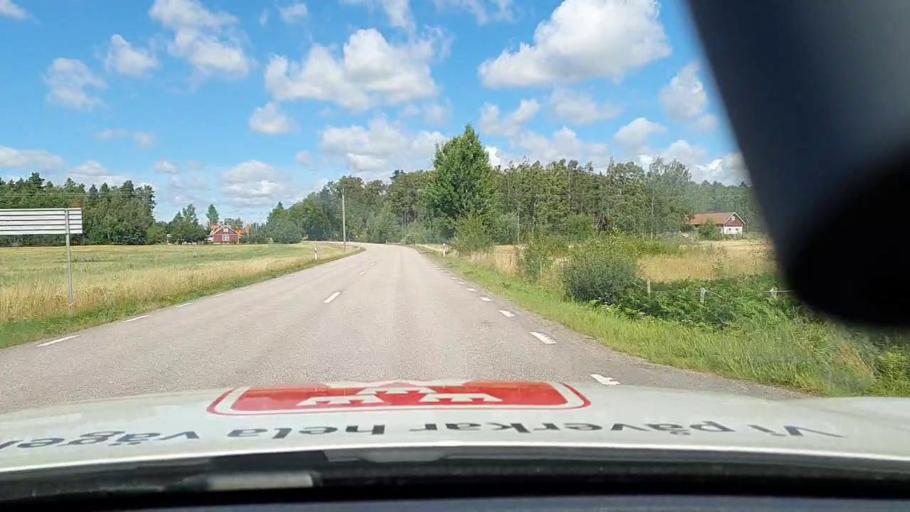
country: SE
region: Vaestra Goetaland
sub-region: Skovde Kommun
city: Stopen
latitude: 58.4988
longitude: 13.9691
